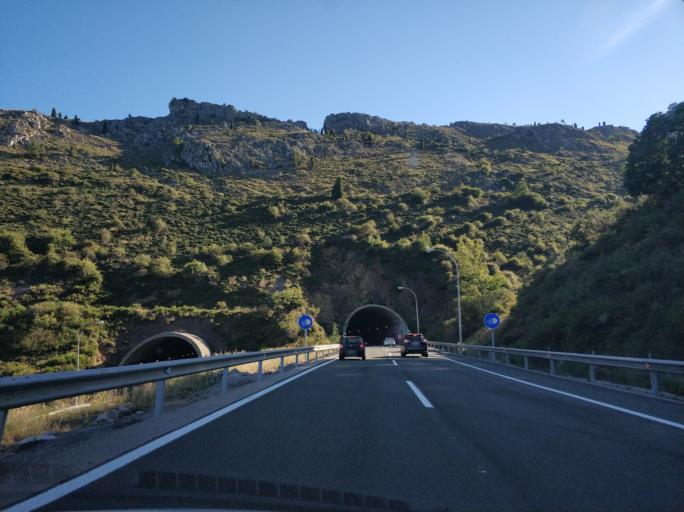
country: ES
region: Castille and Leon
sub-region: Provincia de Leon
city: Sena de Luna
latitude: 42.8876
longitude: -5.8899
